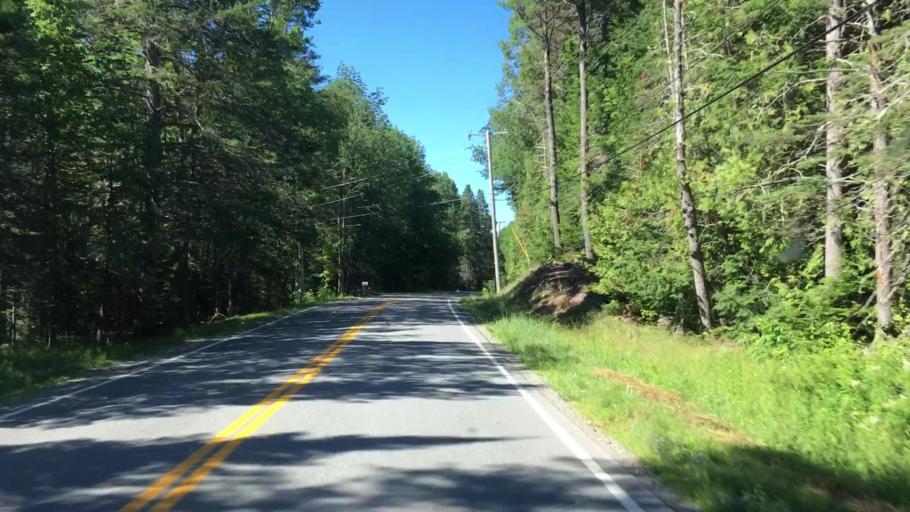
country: US
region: Maine
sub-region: Hancock County
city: Dedham
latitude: 44.7174
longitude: -68.6433
